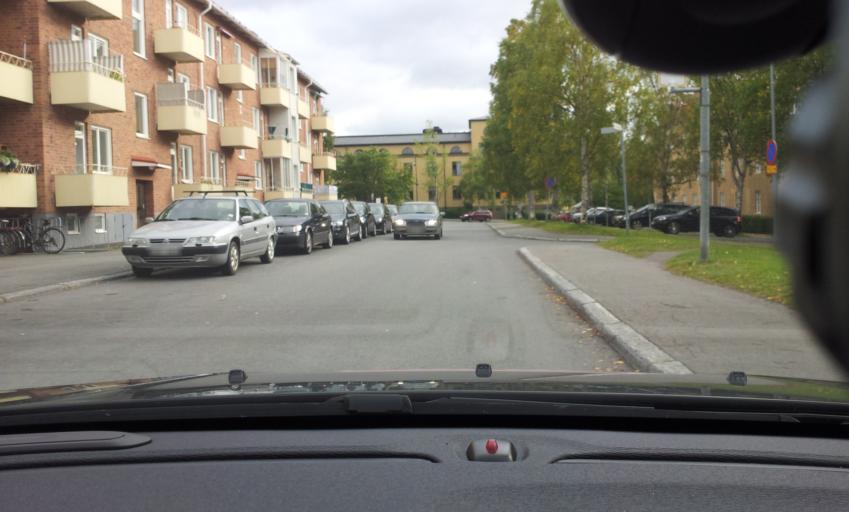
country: SE
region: Jaemtland
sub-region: OEstersunds Kommun
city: Ostersund
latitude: 63.1792
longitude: 14.6475
